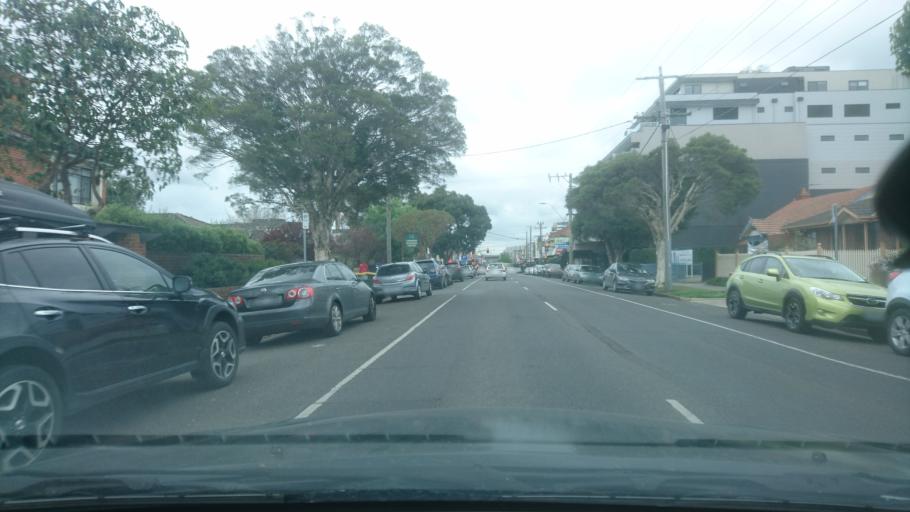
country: AU
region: Victoria
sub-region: Glen Eira
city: Carnegie
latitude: -37.8905
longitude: 145.0568
